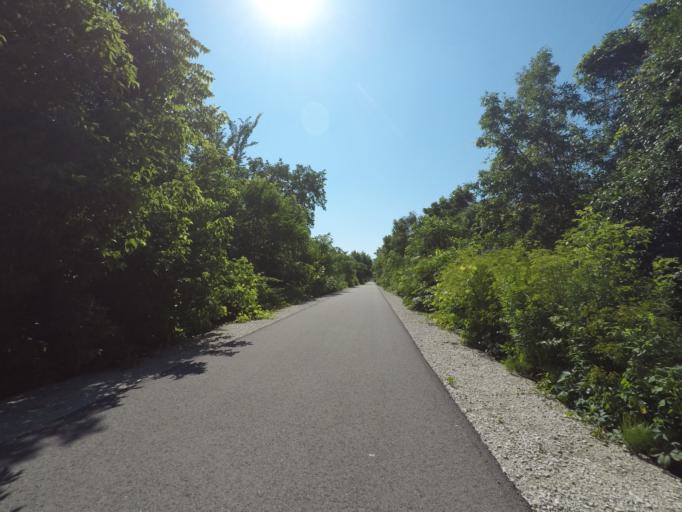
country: US
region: Wisconsin
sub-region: Waukesha County
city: Elm Grove
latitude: 43.0341
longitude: -88.0648
